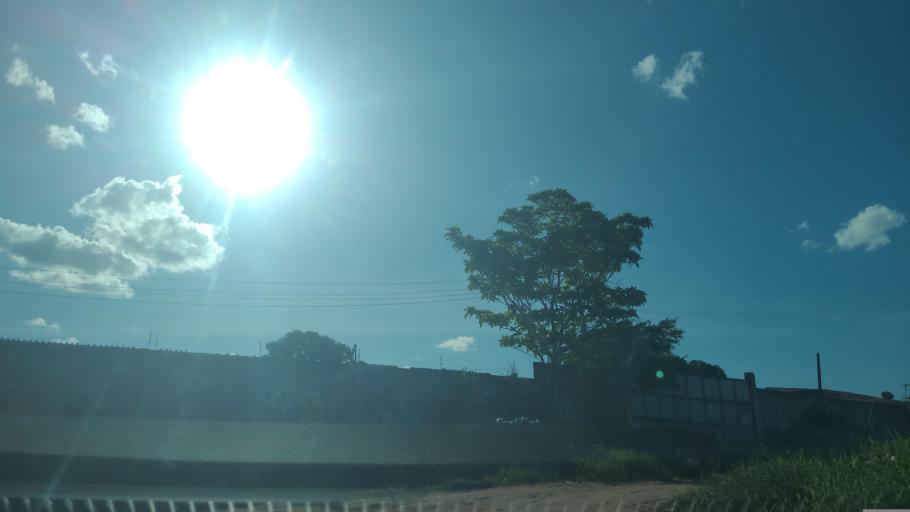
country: BR
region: Alagoas
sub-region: Uniao Dos Palmares
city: Uniao dos Palmares
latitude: -9.1539
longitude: -36.0209
